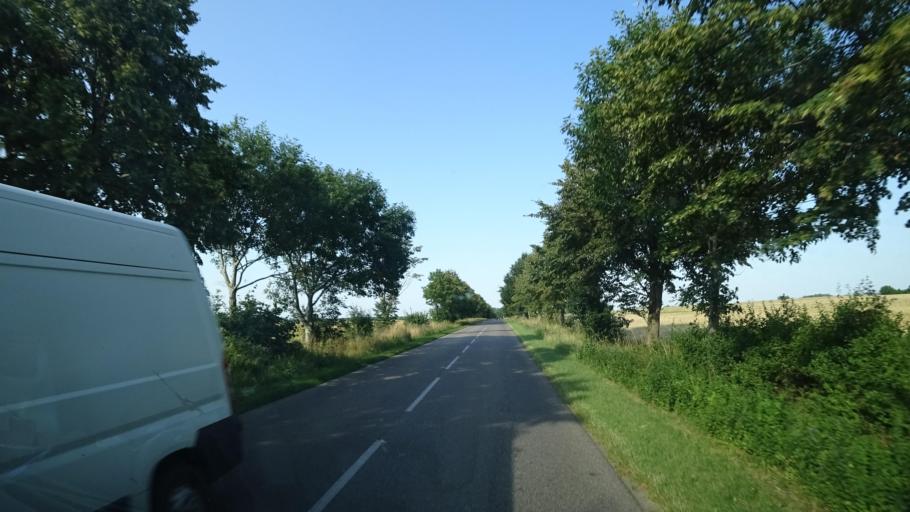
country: PL
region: Pomeranian Voivodeship
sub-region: Powiat czluchowski
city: Przechlewo
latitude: 53.8159
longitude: 17.3615
